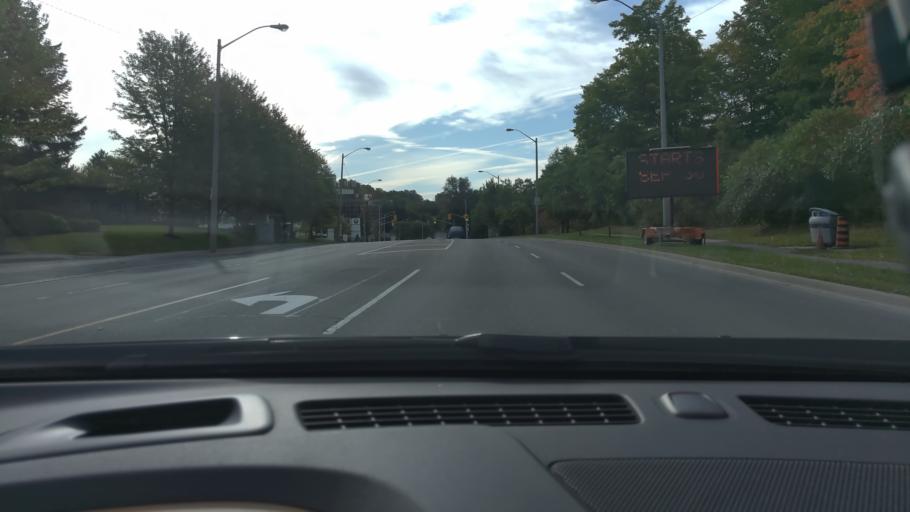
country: CA
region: Ontario
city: Willowdale
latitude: 43.7279
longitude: -79.3520
